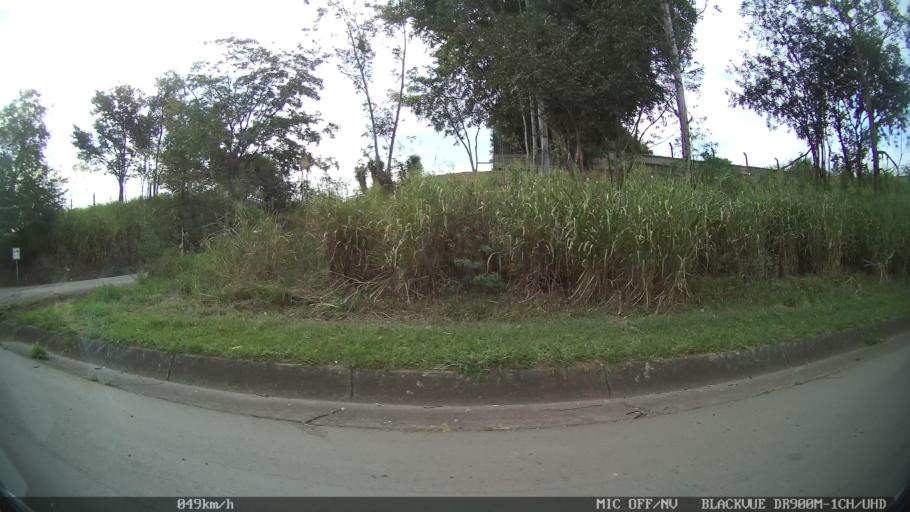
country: BR
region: Sao Paulo
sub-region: Cosmopolis
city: Cosmopolis
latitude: -22.6285
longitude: -47.2767
